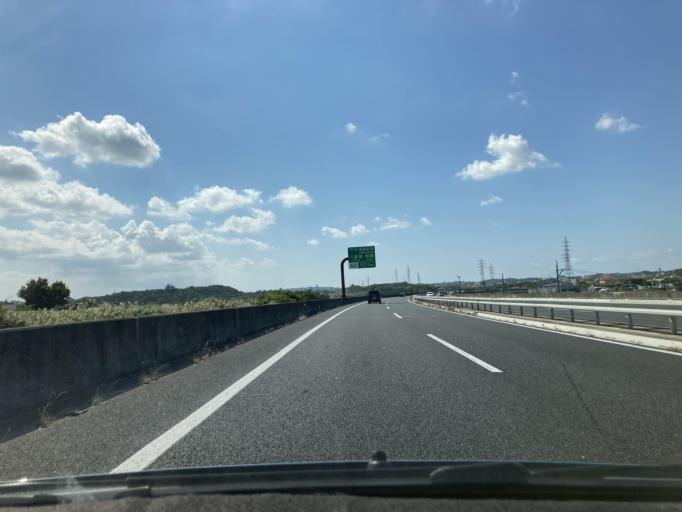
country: JP
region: Okinawa
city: Tomigusuku
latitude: 26.1864
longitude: 127.7369
